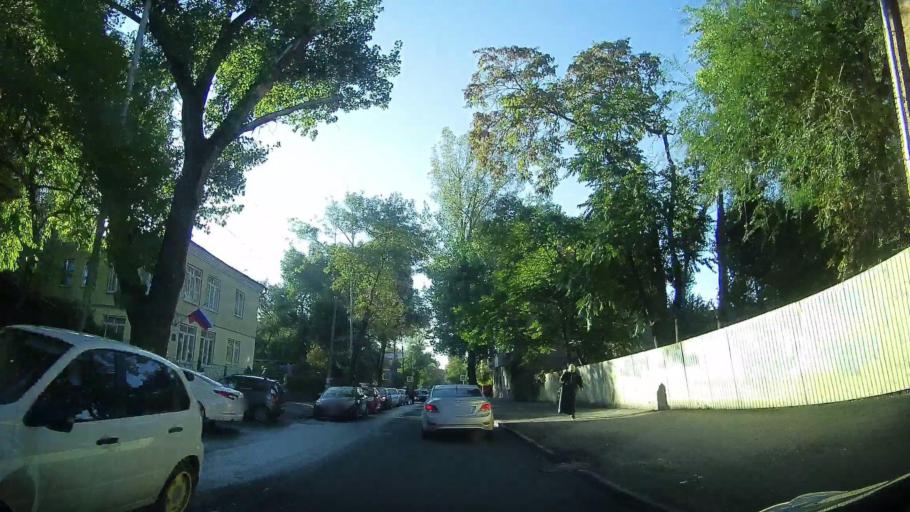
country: RU
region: Rostov
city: Rostov-na-Donu
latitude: 47.2352
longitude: 39.6952
